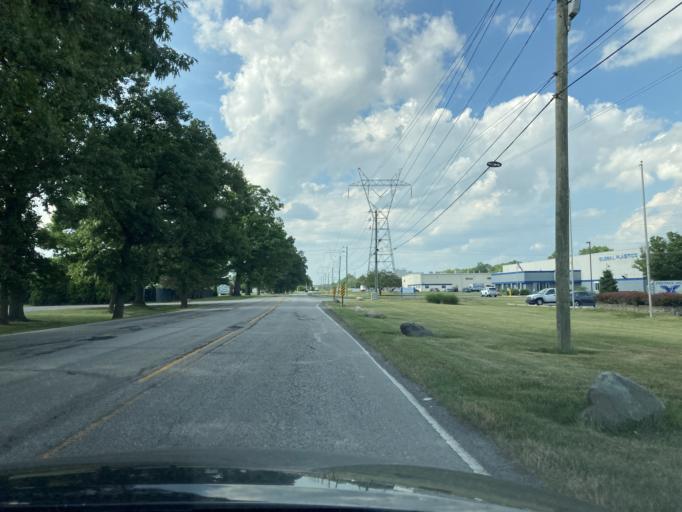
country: US
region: Indiana
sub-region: Marion County
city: Meridian Hills
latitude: 39.8771
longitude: -86.2316
